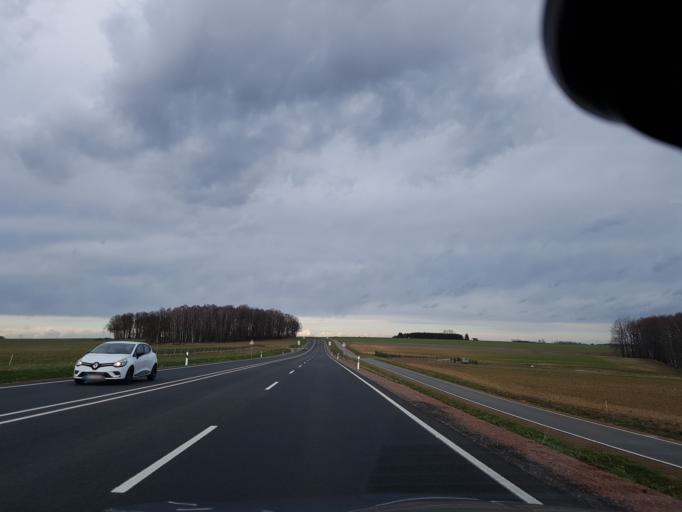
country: DE
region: Saxony
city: Niederstriegis
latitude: 51.0413
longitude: 13.1137
